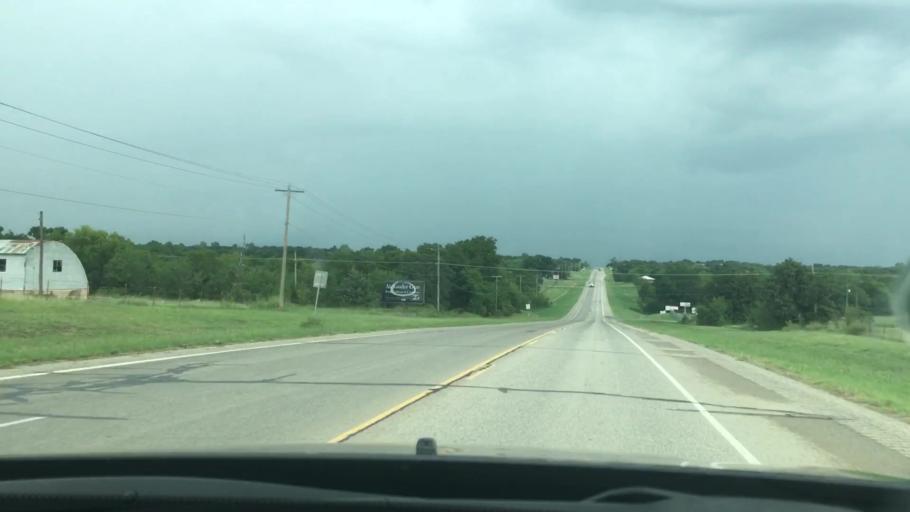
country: US
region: Oklahoma
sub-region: Carter County
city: Healdton
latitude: 34.2035
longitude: -97.4747
